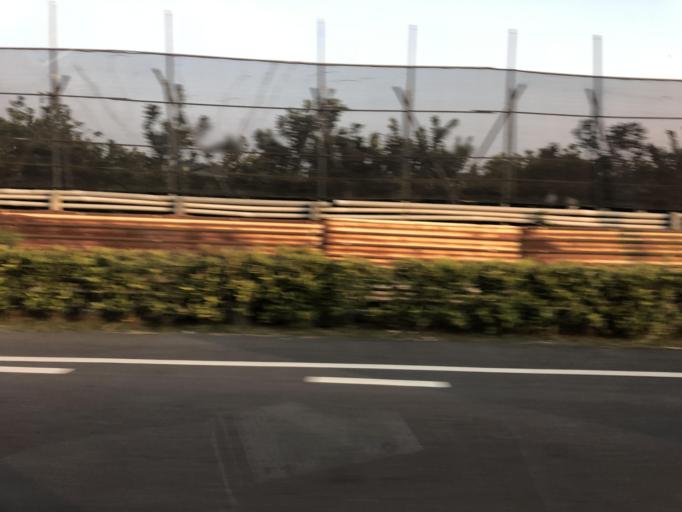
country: TW
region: Taiwan
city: Xinying
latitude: 23.1995
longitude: 120.2670
